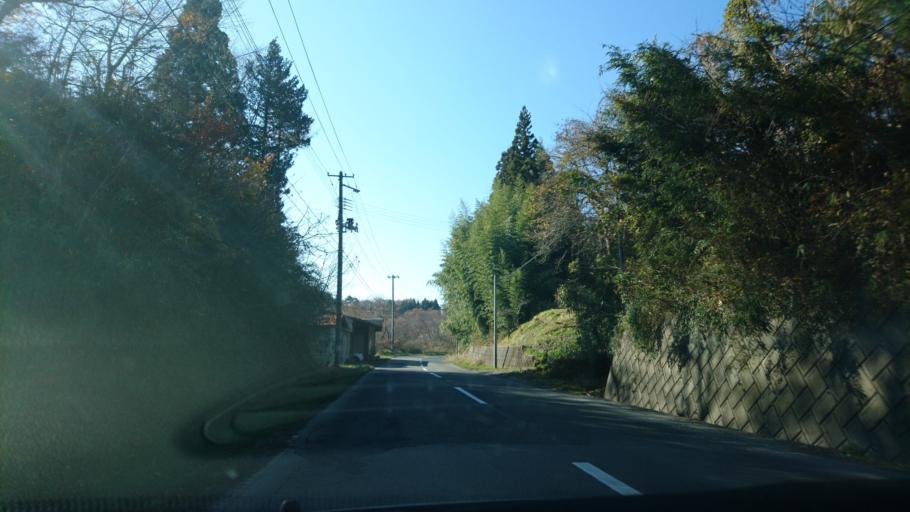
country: JP
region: Iwate
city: Ichinoseki
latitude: 38.9016
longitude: 141.3959
